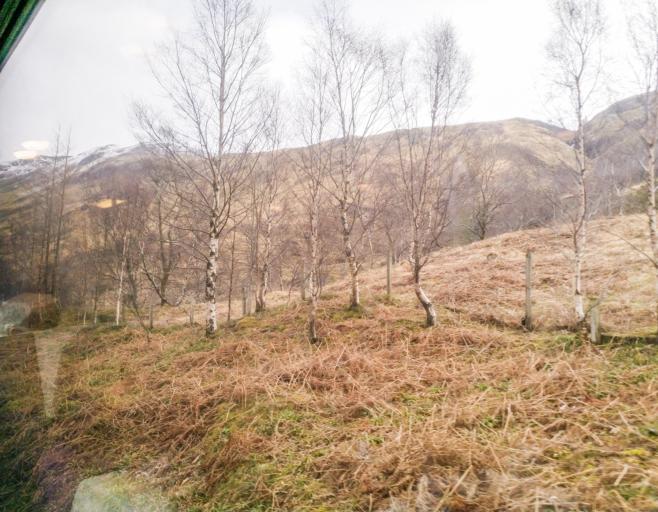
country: GB
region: Scotland
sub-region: Highland
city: Spean Bridge
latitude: 56.8135
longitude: -4.7155
